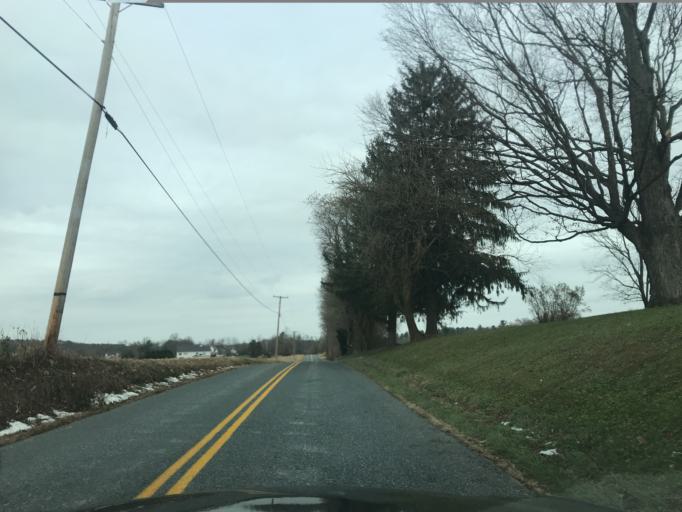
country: US
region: Maryland
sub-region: Harford County
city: Jarrettsville
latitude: 39.6685
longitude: -76.4320
